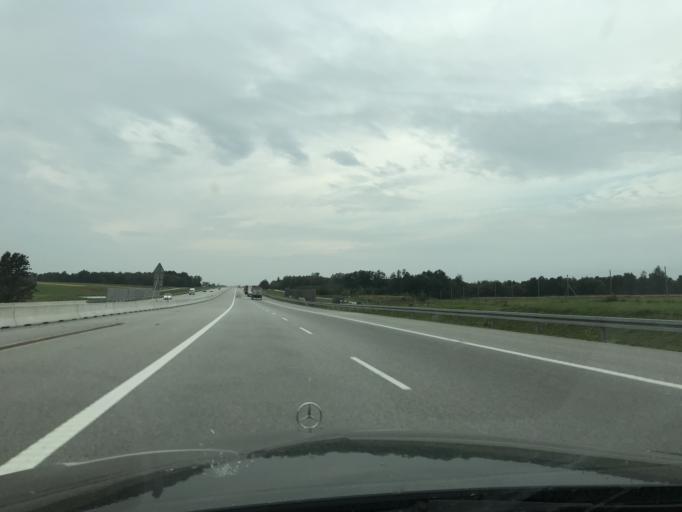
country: PL
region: Subcarpathian Voivodeship
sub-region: Powiat debicki
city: Czarna
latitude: 50.1003
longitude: 21.2751
